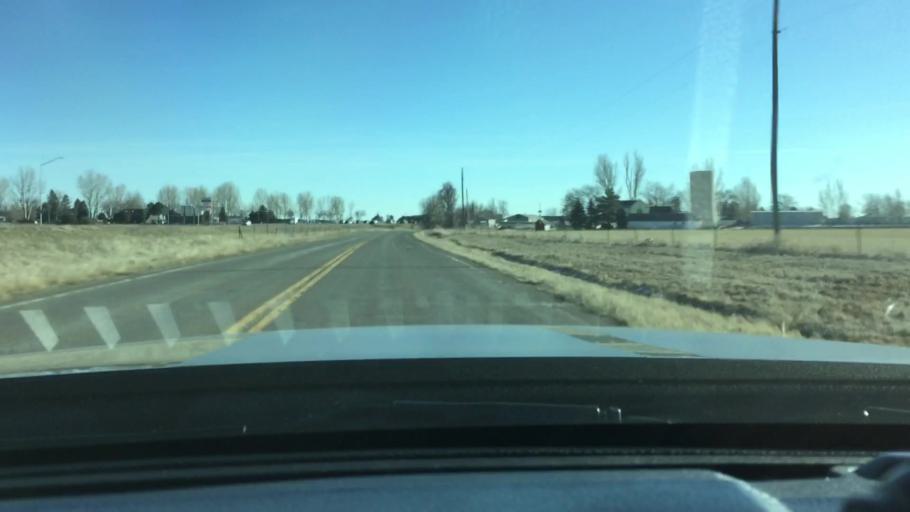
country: US
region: Colorado
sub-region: Weld County
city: Johnstown
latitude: 40.3595
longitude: -104.9844
